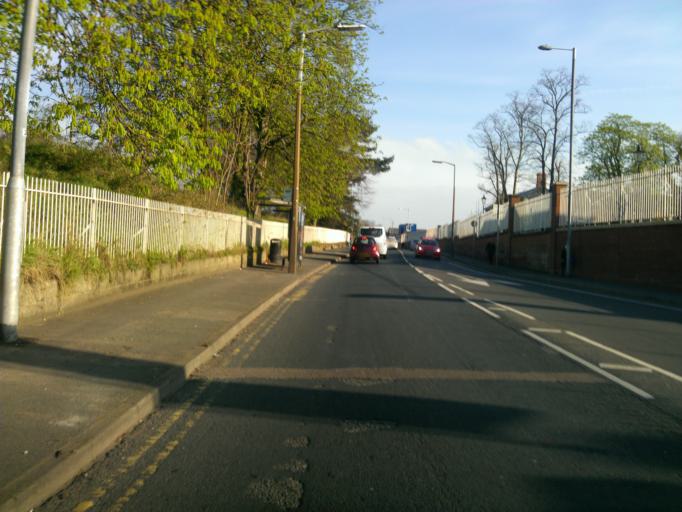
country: GB
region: England
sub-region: Essex
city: Colchester
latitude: 51.8811
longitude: 0.9037
